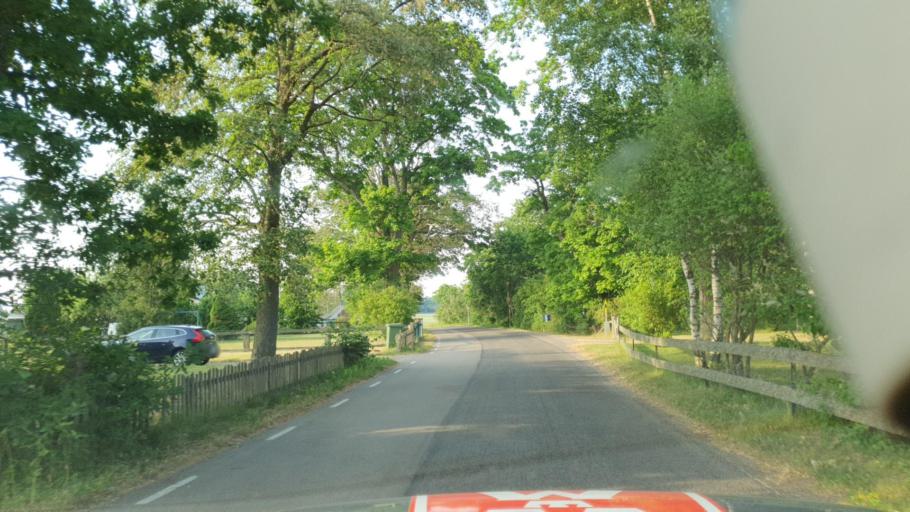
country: SE
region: Kalmar
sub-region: Kalmar Kommun
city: Ljungbyholm
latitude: 56.5084
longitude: 16.1247
